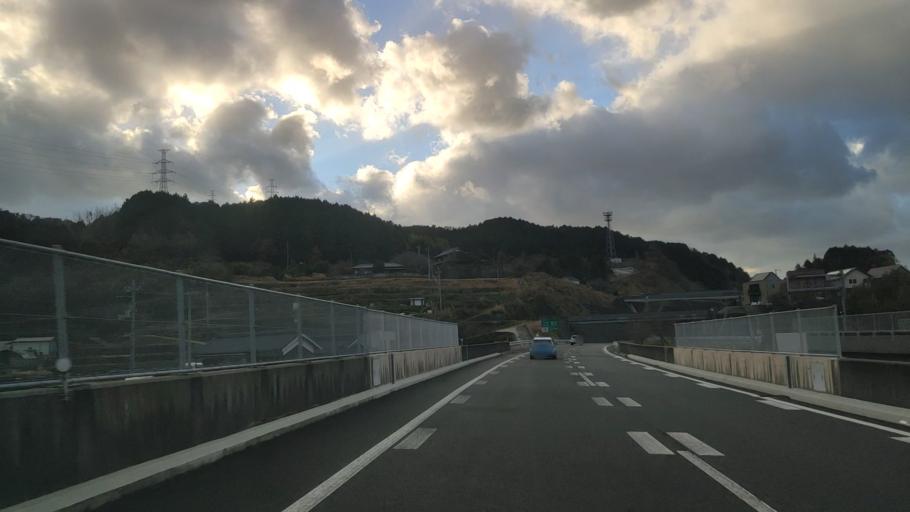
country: JP
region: Ehime
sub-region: Shikoku-chuo Shi
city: Matsuyama
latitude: 33.7900
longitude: 132.9197
